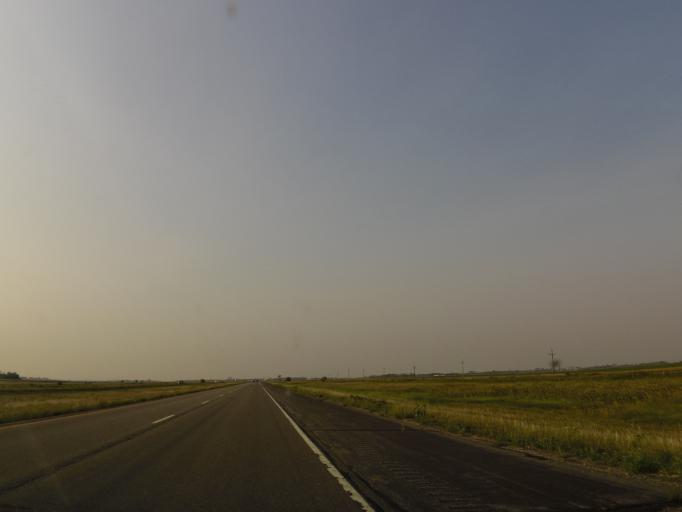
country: US
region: North Dakota
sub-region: Traill County
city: Hillsboro
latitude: 47.2900
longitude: -97.0227
